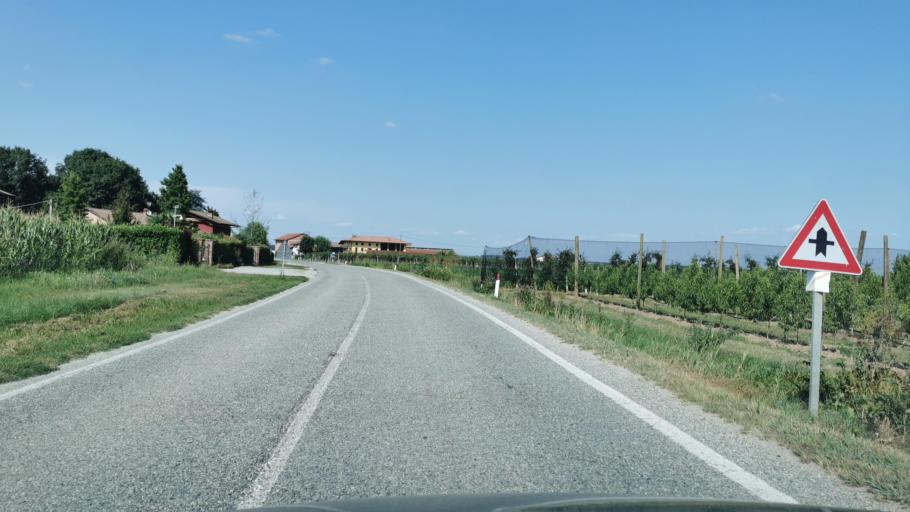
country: IT
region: Piedmont
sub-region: Provincia di Cuneo
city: Revello
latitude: 44.6784
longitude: 7.4099
